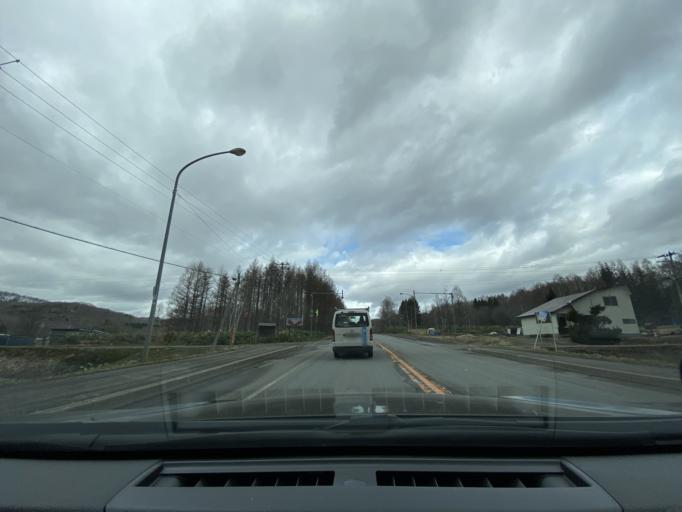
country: JP
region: Hokkaido
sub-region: Asahikawa-shi
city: Asahikawa
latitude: 43.9524
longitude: 142.4542
